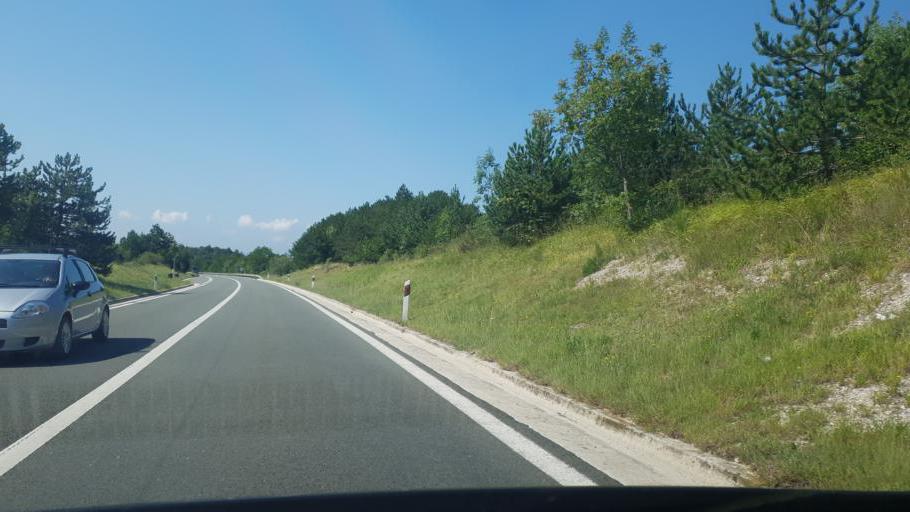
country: HR
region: Istarska
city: Buzet
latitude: 45.3341
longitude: 14.0761
